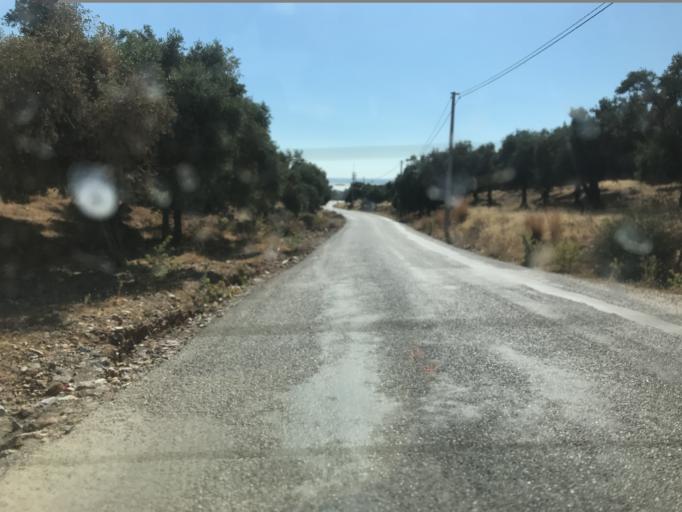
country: TR
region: Aydin
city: Sarikemer
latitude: 37.3934
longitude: 27.4593
